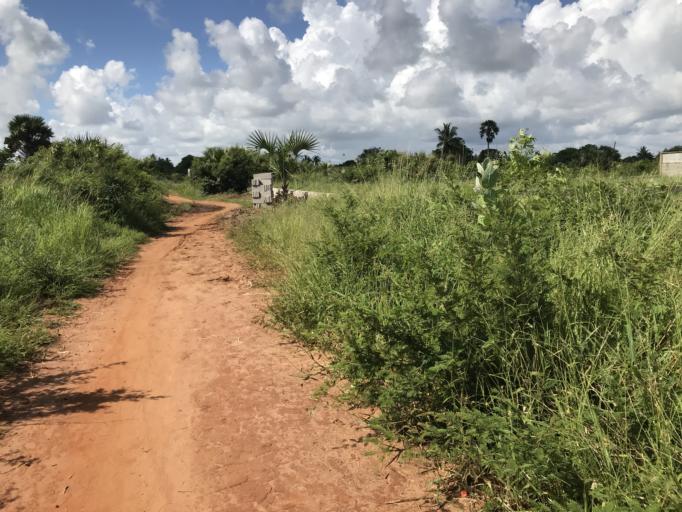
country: TZ
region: Dar es Salaam
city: Dar es Salaam
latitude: -6.8820
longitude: 39.4390
